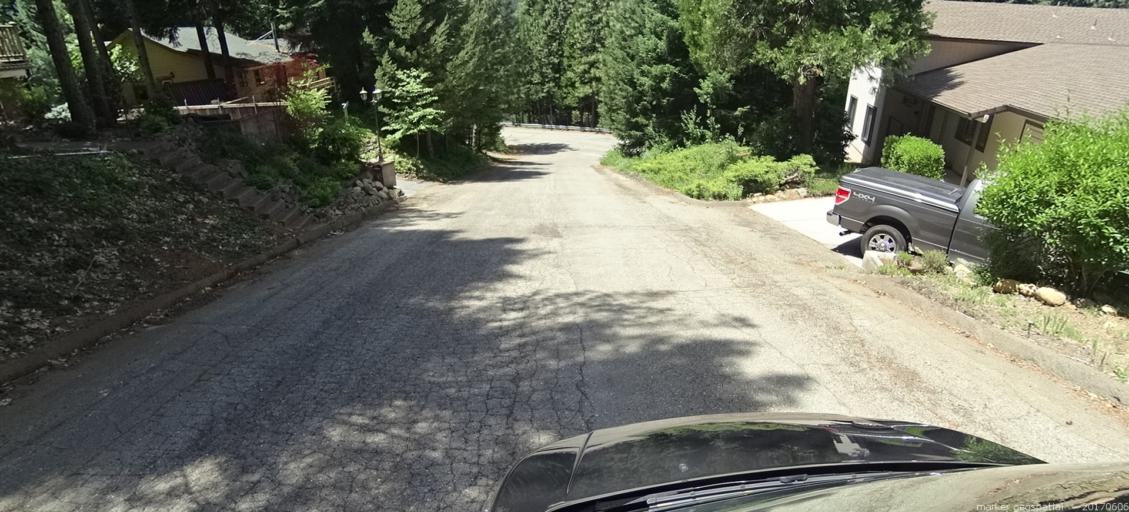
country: US
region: California
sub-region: Siskiyou County
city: Dunsmuir
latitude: 41.2311
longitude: -122.2726
